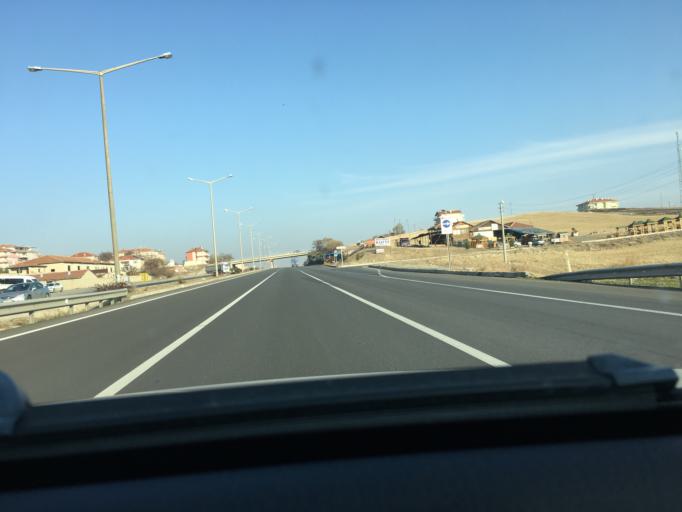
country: TR
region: Ankara
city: Temelli
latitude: 39.7232
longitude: 32.3473
